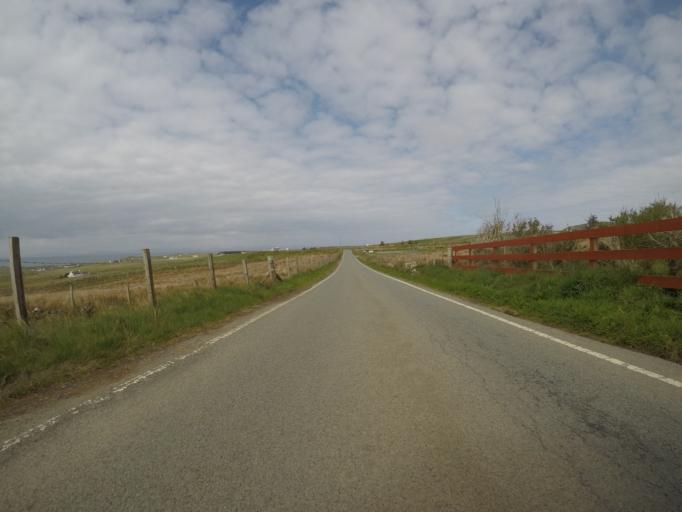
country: GB
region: Scotland
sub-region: Highland
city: Portree
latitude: 57.6399
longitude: -6.3765
